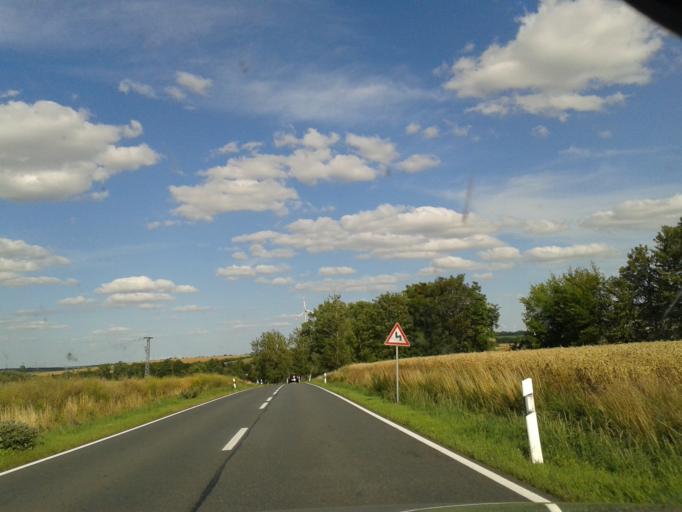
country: DE
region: Saxony-Anhalt
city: Polleben
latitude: 51.5797
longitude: 11.5870
